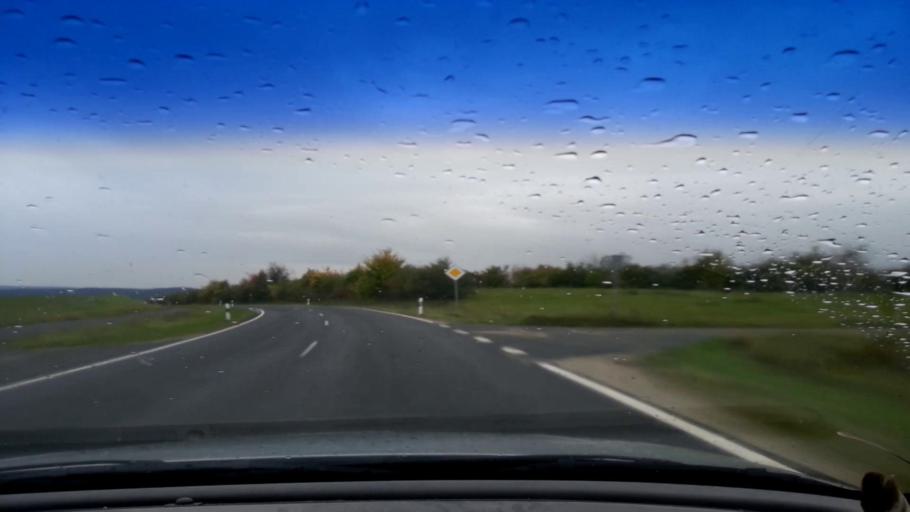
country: DE
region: Bavaria
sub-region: Upper Franconia
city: Priesendorf
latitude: 49.8697
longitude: 10.7160
